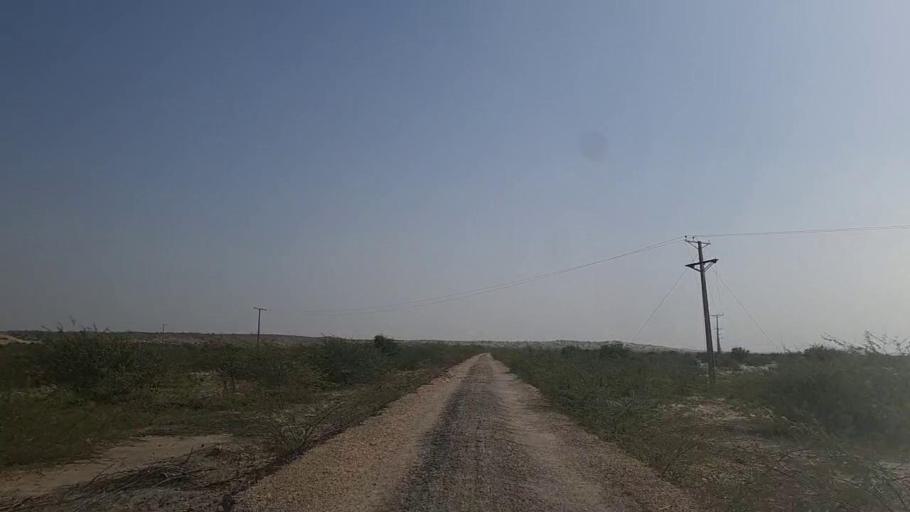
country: PK
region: Sindh
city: Naukot
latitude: 24.5869
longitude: 69.2926
